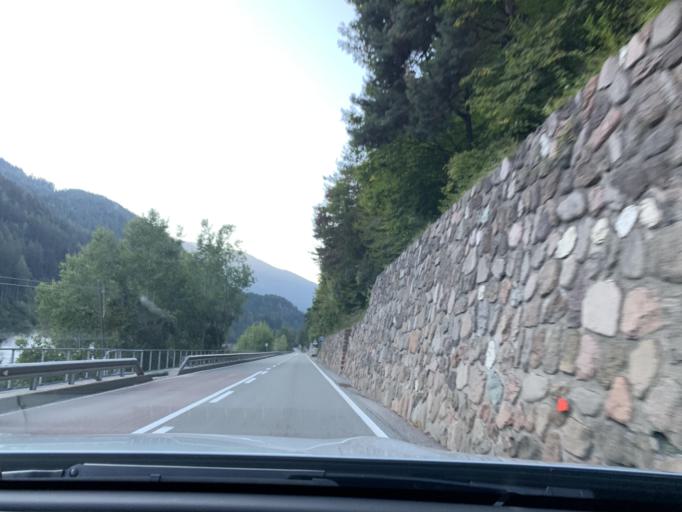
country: IT
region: Trentino-Alto Adige
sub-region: Bolzano
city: Nova Ponente
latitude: 46.4461
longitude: 11.4568
